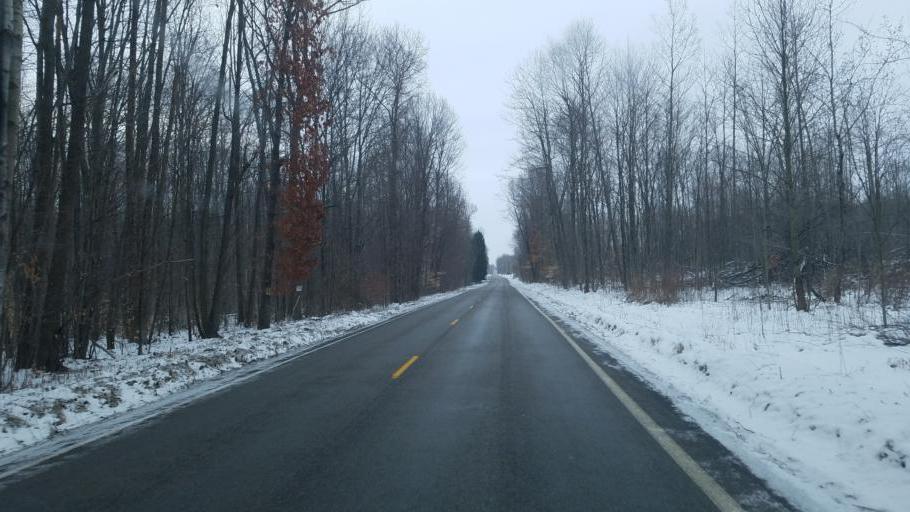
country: US
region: Pennsylvania
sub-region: Mercer County
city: Stoneboro
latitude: 41.4079
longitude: -80.0506
